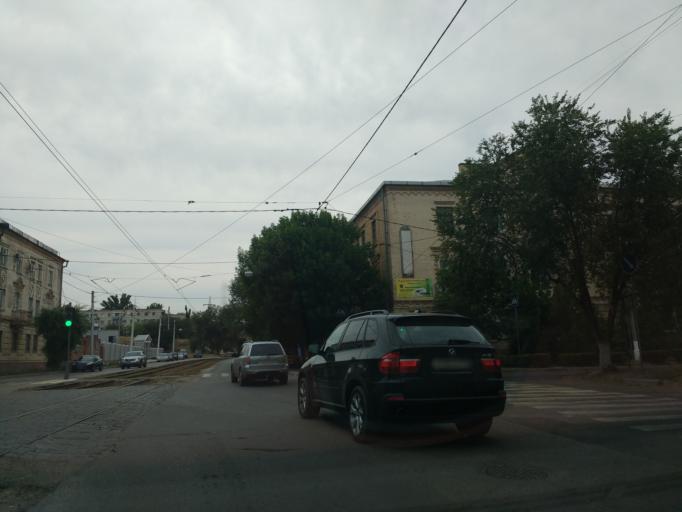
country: RU
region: Volgograd
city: Volgograd
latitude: 48.6958
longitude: 44.4888
